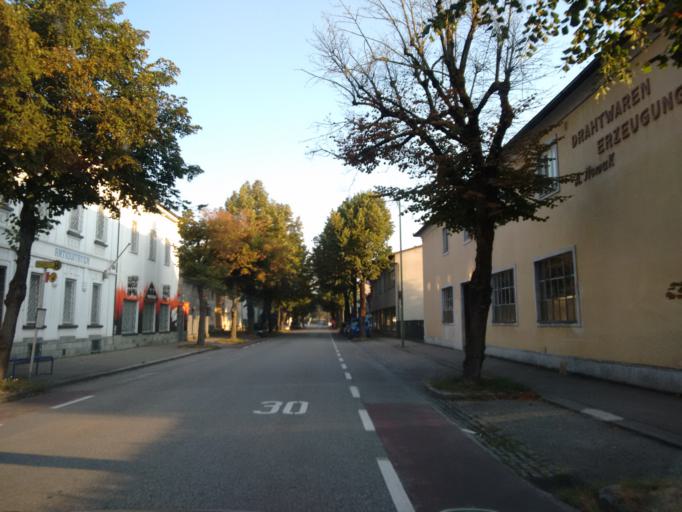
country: AT
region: Upper Austria
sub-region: Wels Stadt
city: Wels
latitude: 48.1682
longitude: 14.0226
